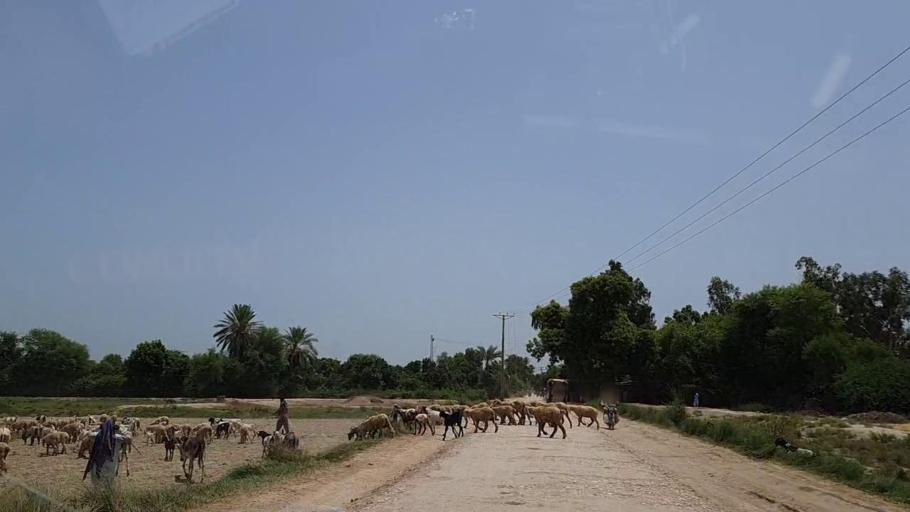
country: PK
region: Sindh
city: Tharu Shah
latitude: 26.9474
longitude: 68.1037
